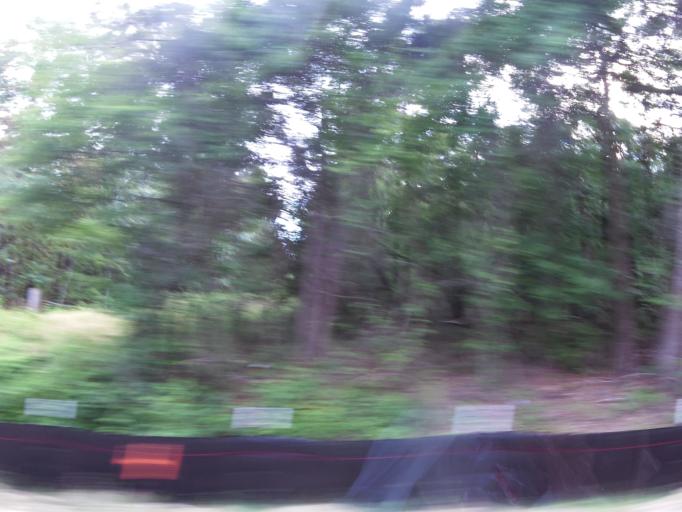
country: US
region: South Carolina
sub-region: Jasper County
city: Ridgeland
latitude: 32.4780
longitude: -81.1154
